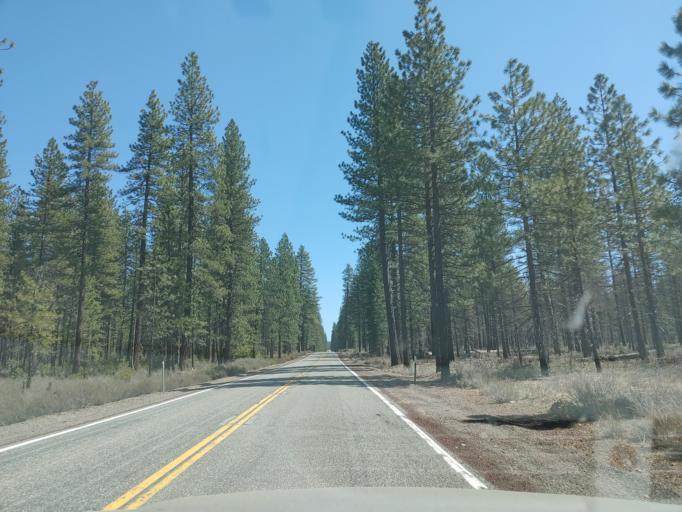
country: US
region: California
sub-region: Siskiyou County
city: McCloud
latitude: 41.2638
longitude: -121.9420
